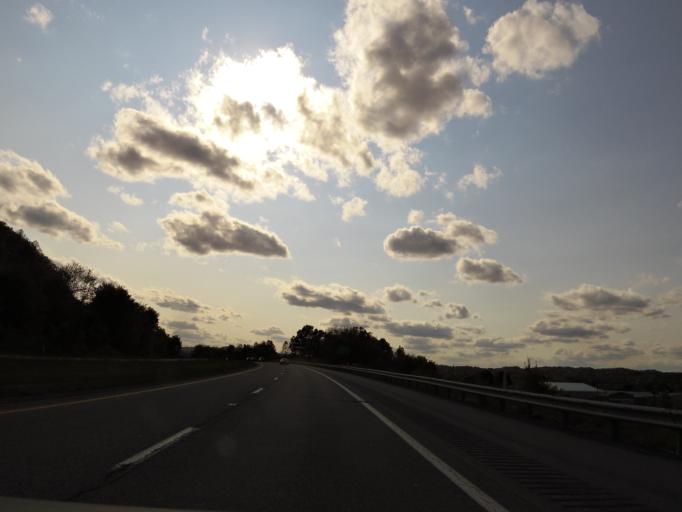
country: US
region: West Virginia
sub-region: Mercer County
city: Princeton
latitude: 37.3626
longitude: -81.0697
